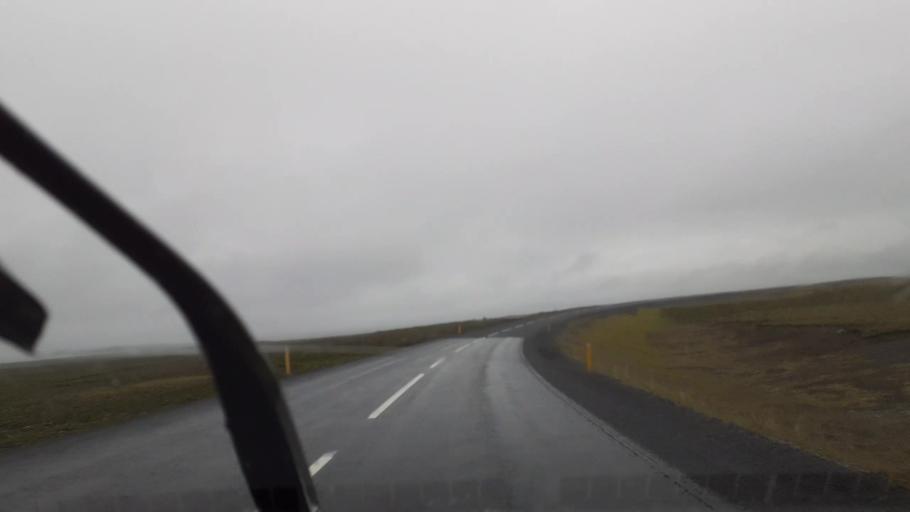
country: IS
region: Northeast
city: Husavik
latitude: 66.2387
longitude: -15.7516
